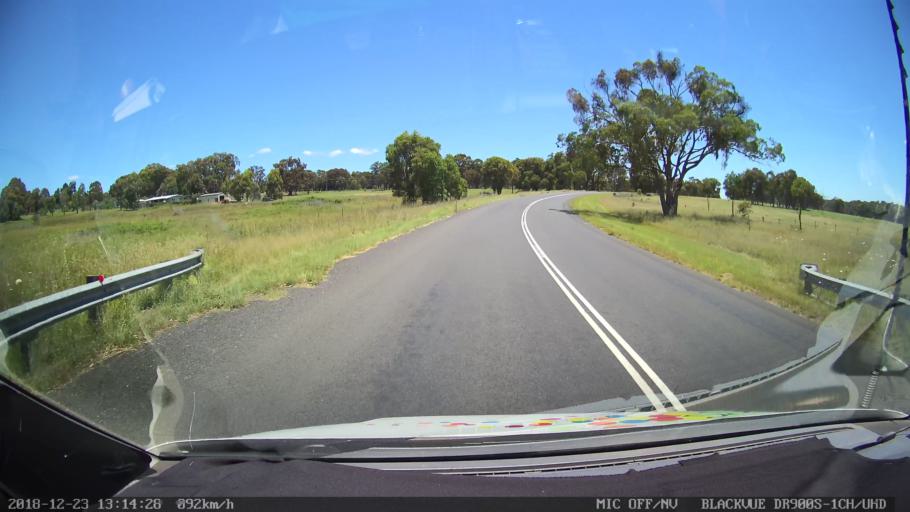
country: AU
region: New South Wales
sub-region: Armidale Dumaresq
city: Armidale
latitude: -30.5045
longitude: 151.5269
